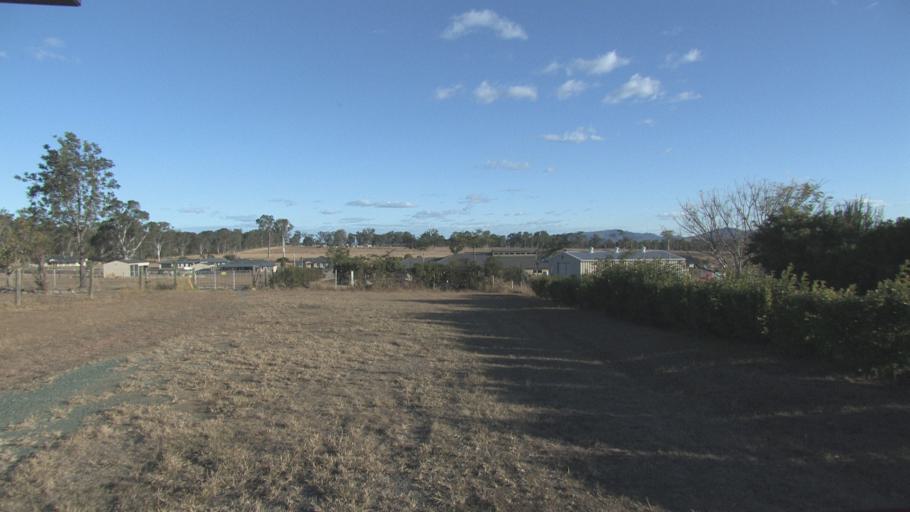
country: AU
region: Queensland
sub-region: Logan
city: Cedar Vale
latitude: -27.8717
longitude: 152.9725
